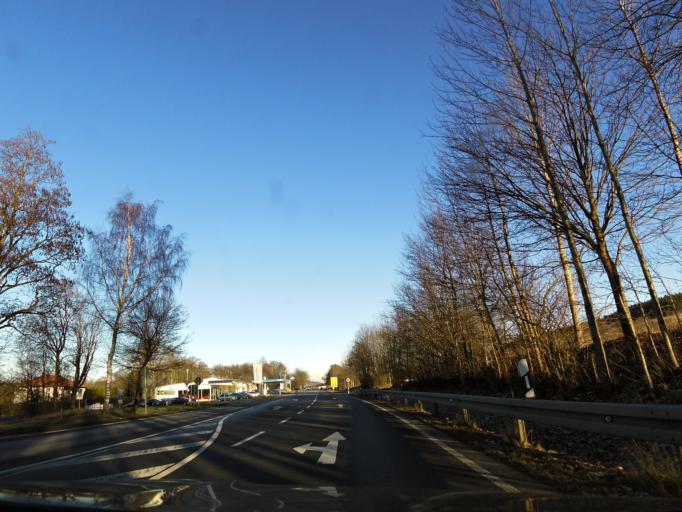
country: DE
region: Bavaria
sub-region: Upper Franconia
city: Trostau
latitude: 50.0150
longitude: 11.9562
